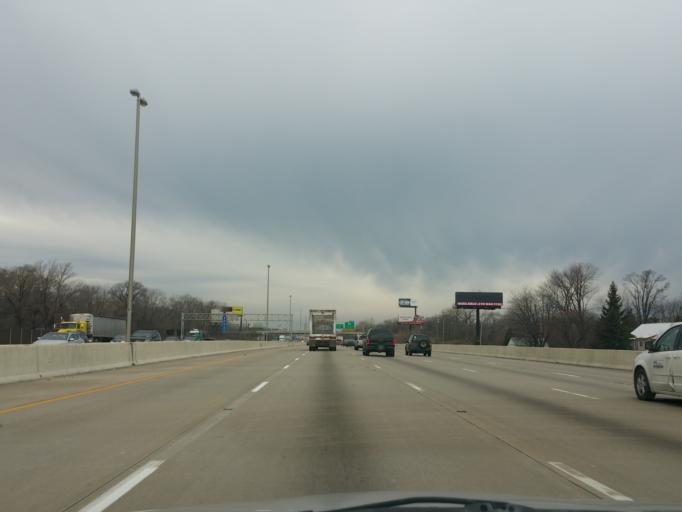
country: US
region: Indiana
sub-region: Lake County
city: Griffith
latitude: 41.5700
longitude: -87.4072
